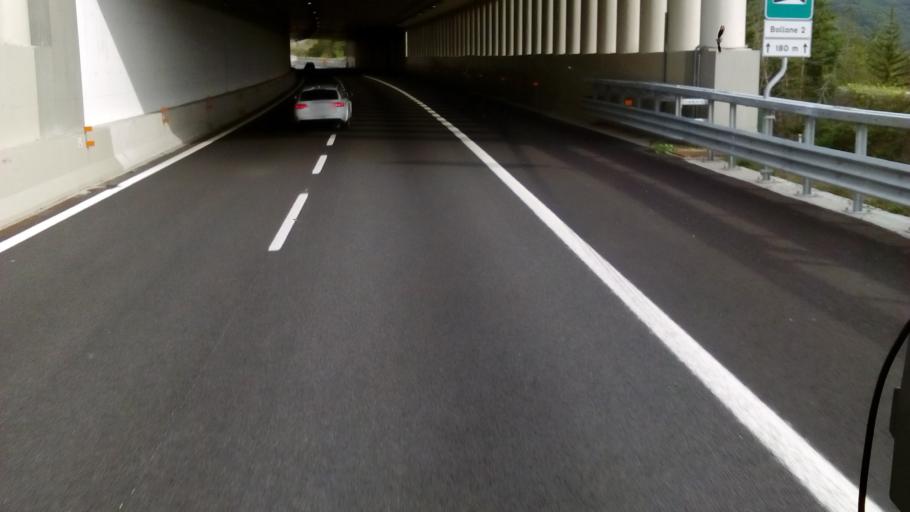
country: IT
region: Tuscany
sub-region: Province of Florence
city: Barberino di Mugello
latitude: 44.0599
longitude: 11.2450
